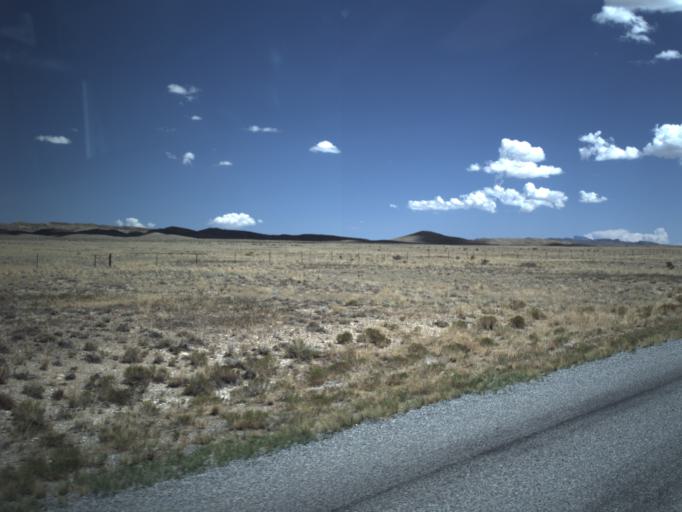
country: US
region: Nevada
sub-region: White Pine County
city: McGill
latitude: 39.0413
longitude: -113.8431
